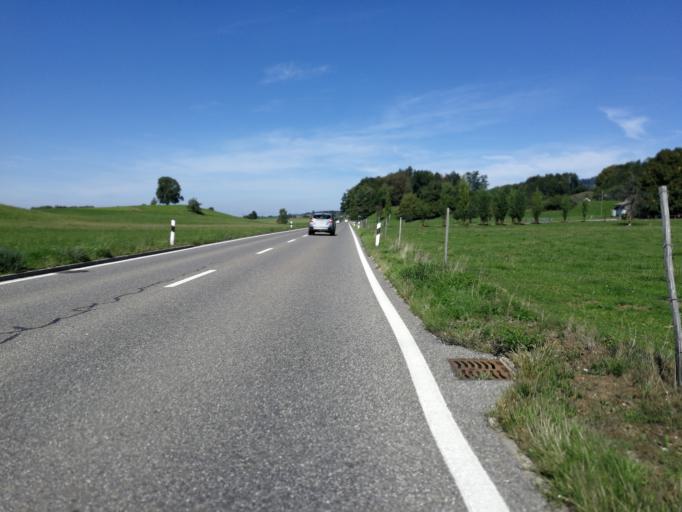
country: CH
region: Zurich
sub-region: Bezirk Hinwil
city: Hinwil
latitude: 47.3118
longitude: 8.8287
